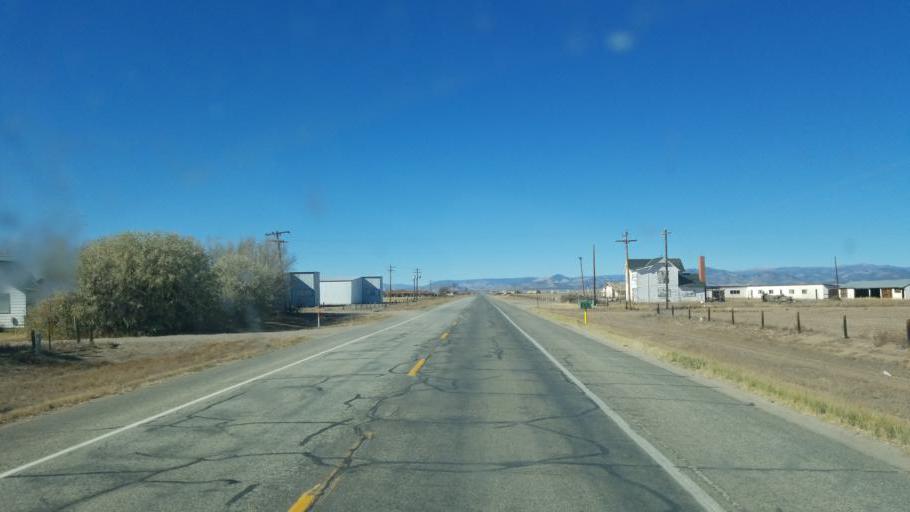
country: US
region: Colorado
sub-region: Saguache County
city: Center
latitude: 37.7482
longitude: -106.1295
